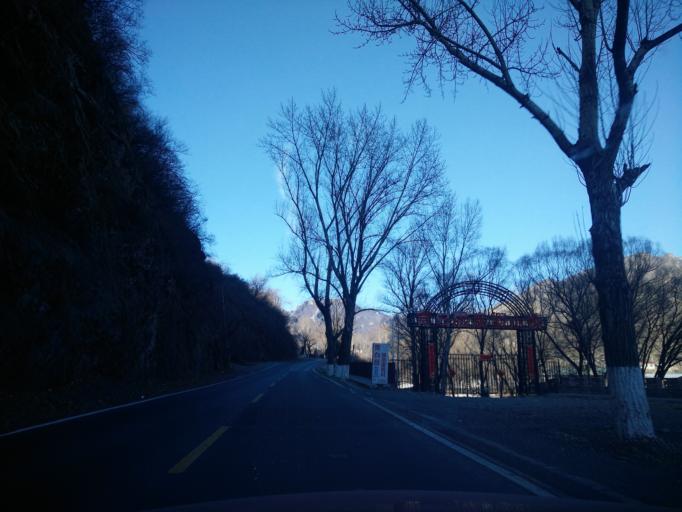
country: CN
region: Beijing
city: Yanchi
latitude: 40.0118
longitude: 115.8226
